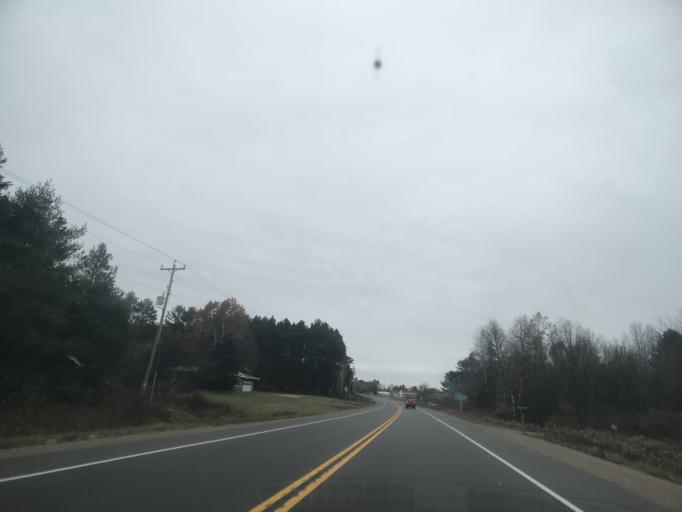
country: US
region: Wisconsin
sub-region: Menominee County
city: Legend Lake
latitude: 45.2959
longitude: -88.5144
